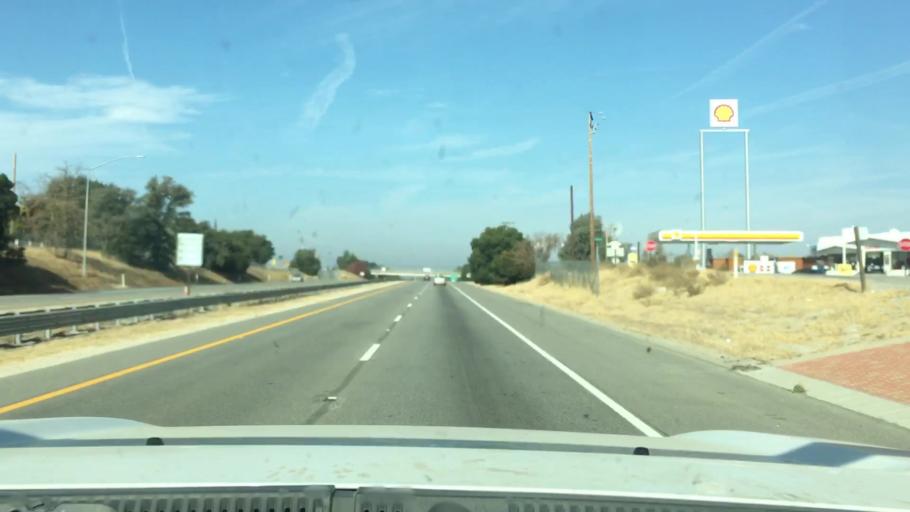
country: US
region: California
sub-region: San Luis Obispo County
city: Atascadero
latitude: 35.4627
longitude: -120.6480
